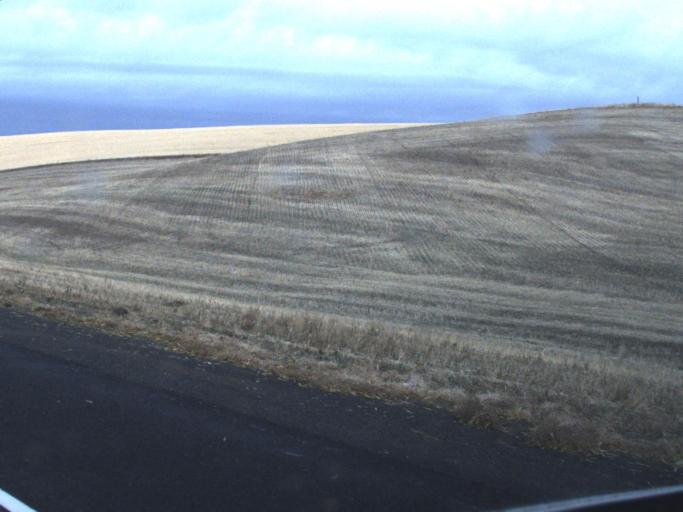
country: US
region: Washington
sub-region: Whitman County
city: Pullman
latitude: 46.6265
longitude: -117.1711
